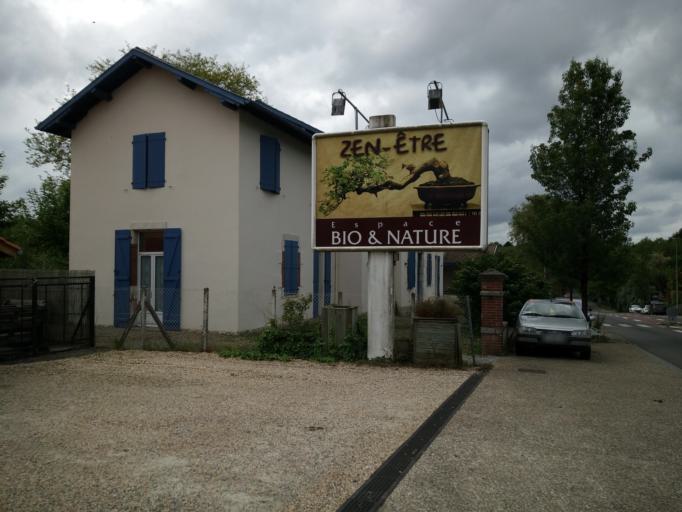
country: FR
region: Aquitaine
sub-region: Departement des Landes
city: Saint-Martin-de-Seignanx
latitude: 43.5278
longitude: -1.3918
